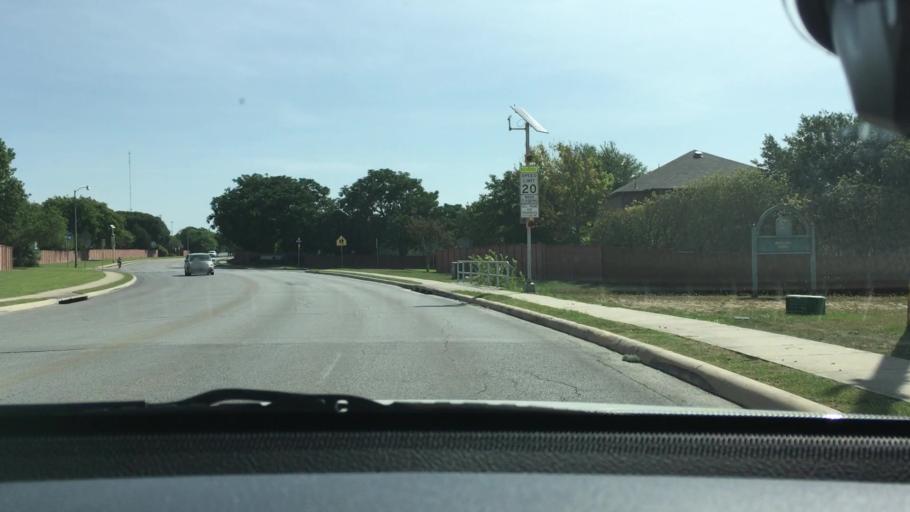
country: US
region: Texas
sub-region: Bexar County
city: Live Oak
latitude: 29.5904
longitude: -98.3949
